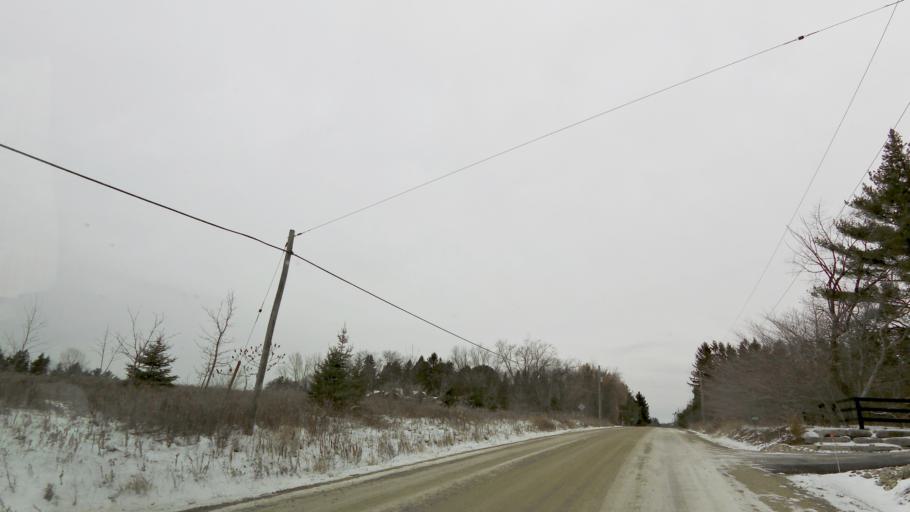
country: CA
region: Ontario
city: Vaughan
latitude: 43.9402
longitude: -79.6101
